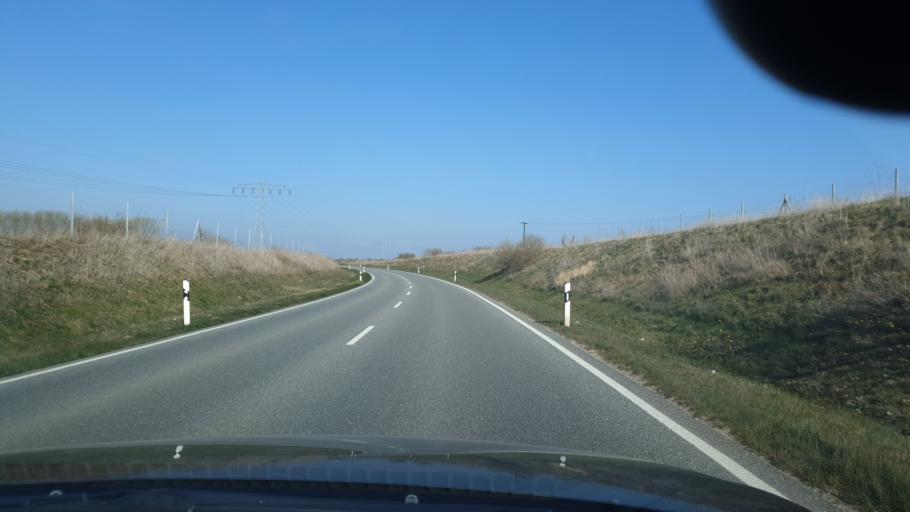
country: DE
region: Mecklenburg-Vorpommern
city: Lankow
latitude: 53.6664
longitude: 11.3685
